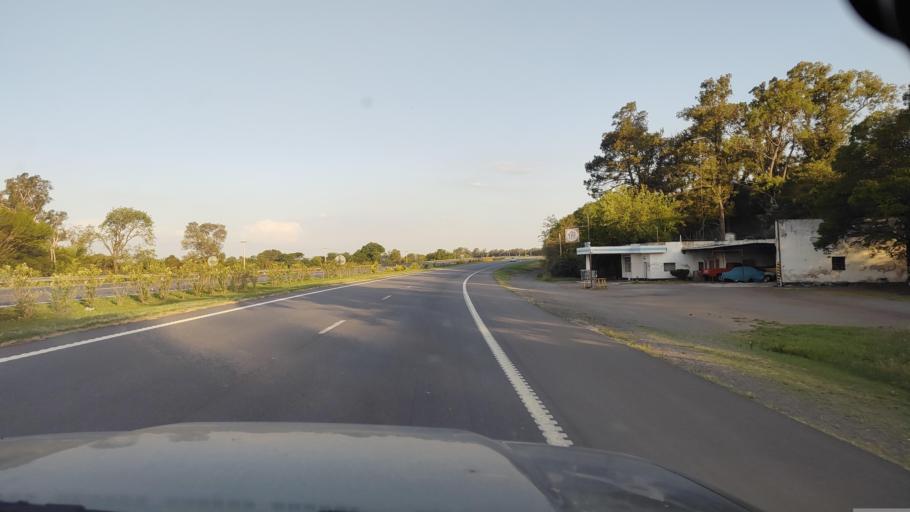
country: AR
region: Buenos Aires
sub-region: Partido de Lujan
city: Lujan
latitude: -34.5473
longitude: -59.2015
